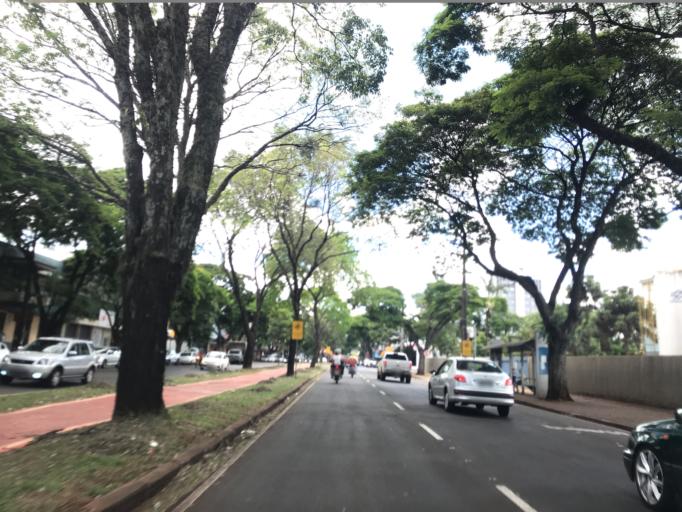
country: BR
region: Parana
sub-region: Maringa
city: Maringa
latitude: -23.4105
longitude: -51.9243
